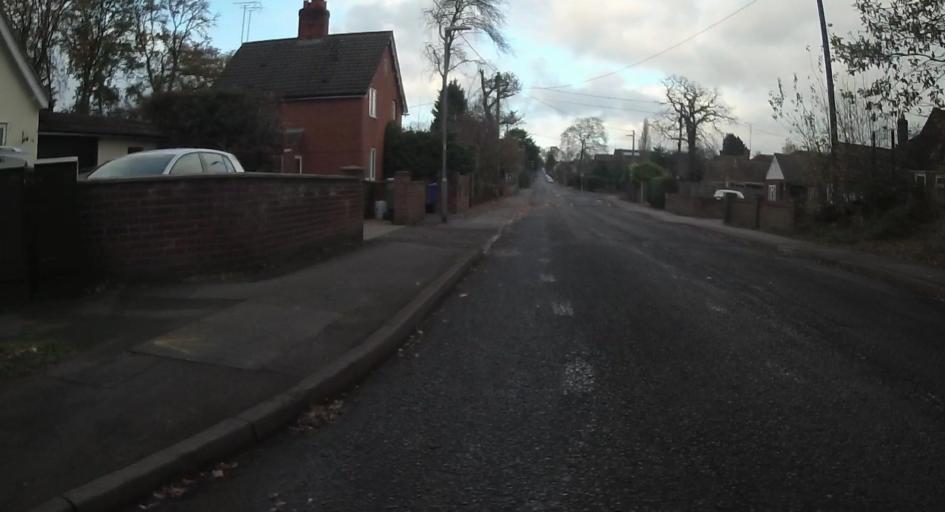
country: GB
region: England
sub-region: Bracknell Forest
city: Sandhurst
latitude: 51.3519
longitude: -0.7821
